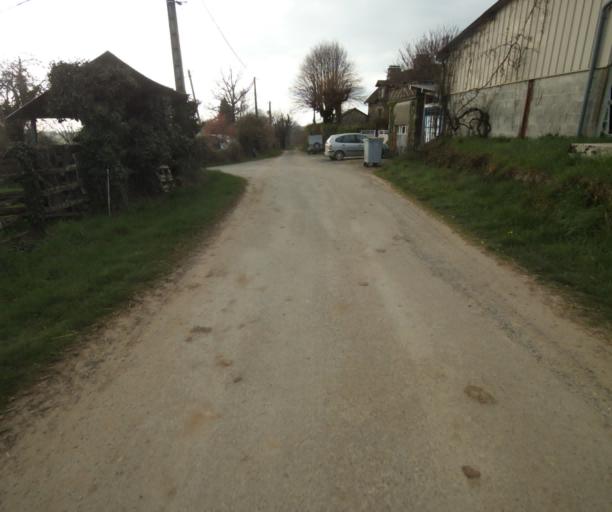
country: FR
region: Limousin
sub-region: Departement de la Correze
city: Saint-Clement
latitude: 45.3652
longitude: 1.6315
